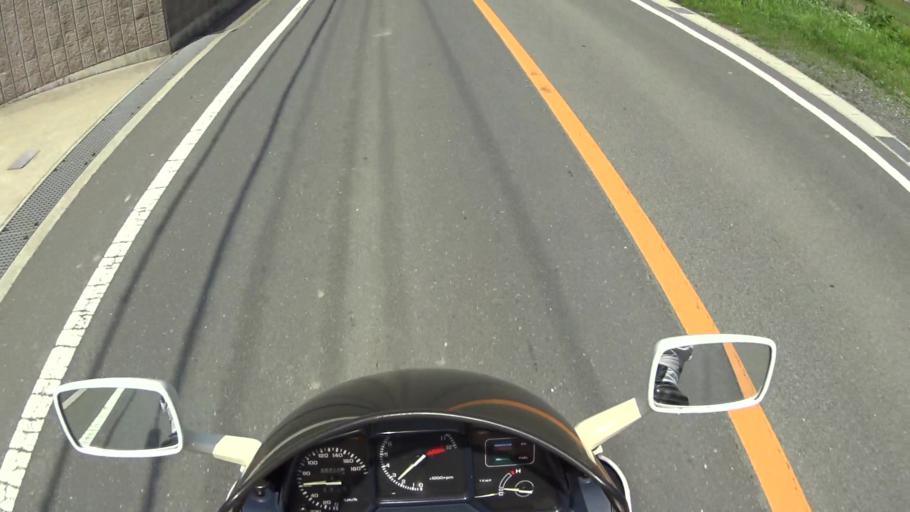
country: JP
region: Kyoto
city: Kameoka
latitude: 35.0088
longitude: 135.4842
